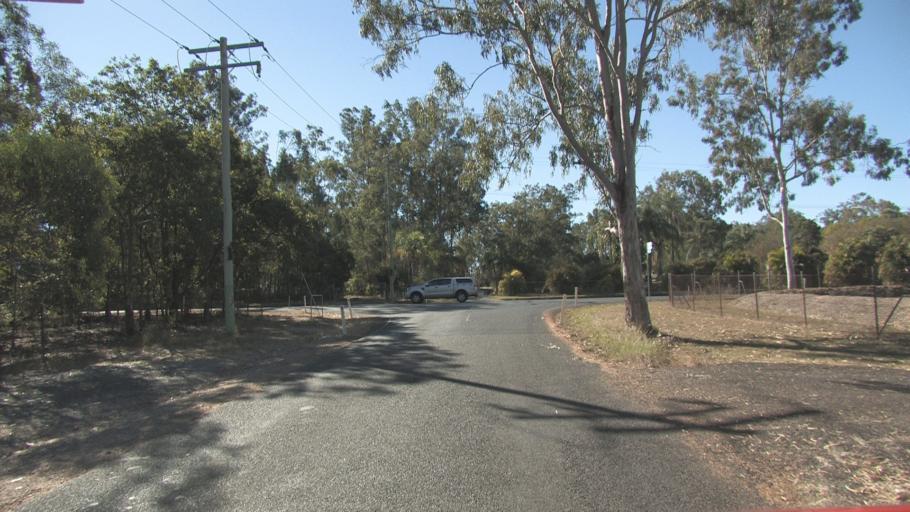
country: AU
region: Queensland
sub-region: Logan
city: Park Ridge South
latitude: -27.7215
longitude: 152.9914
